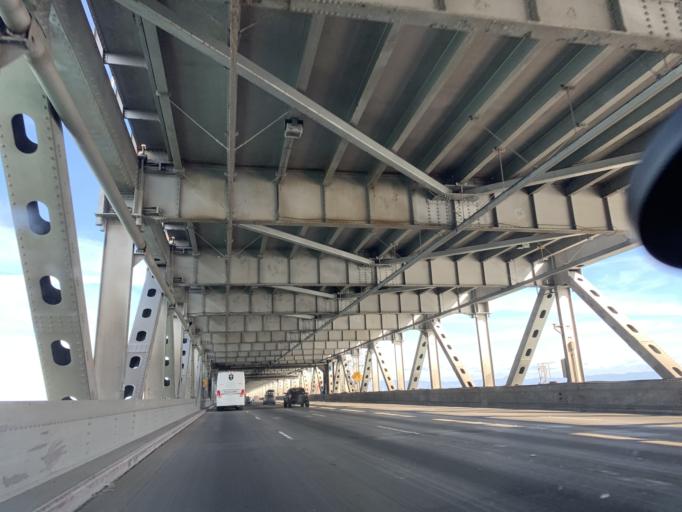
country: US
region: California
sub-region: San Francisco County
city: San Francisco
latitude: 37.7945
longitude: -122.3810
